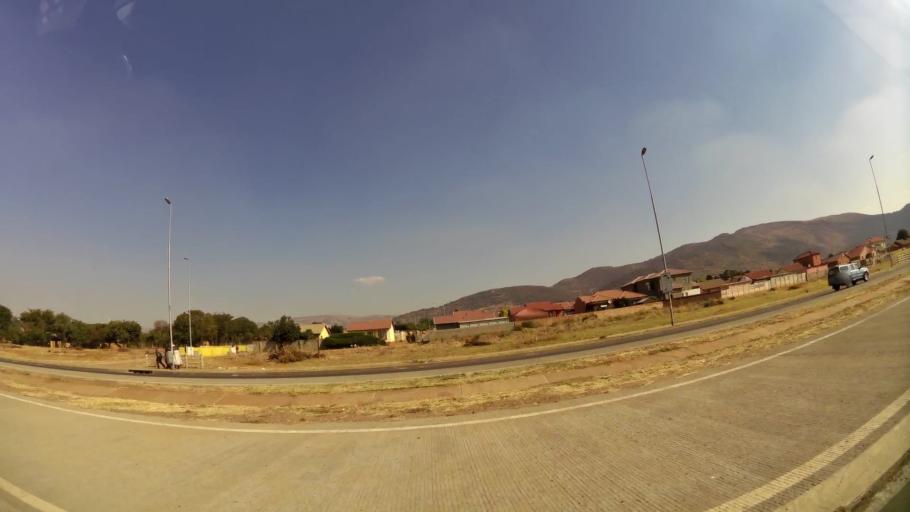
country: ZA
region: North-West
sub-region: Bojanala Platinum District Municipality
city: Rustenburg
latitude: -25.6482
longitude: 27.2128
